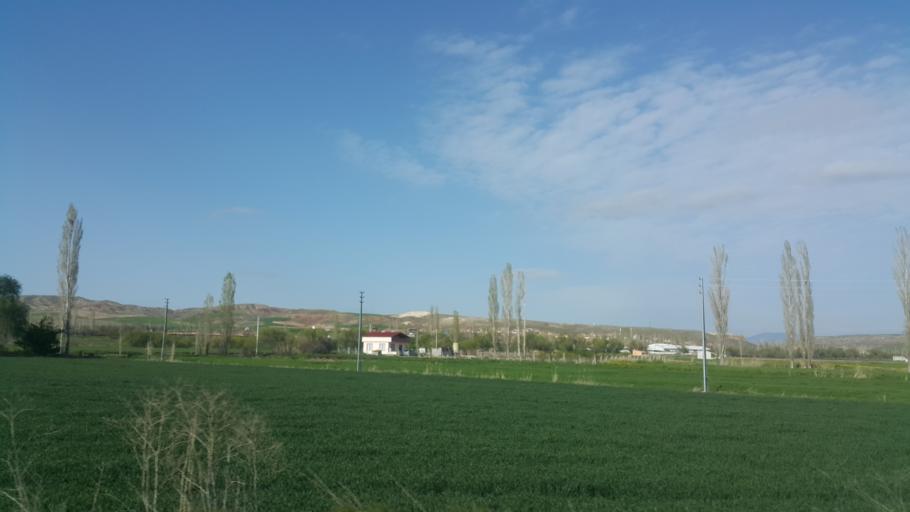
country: TR
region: Aksaray
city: Acipinar
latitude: 38.4800
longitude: 33.8922
